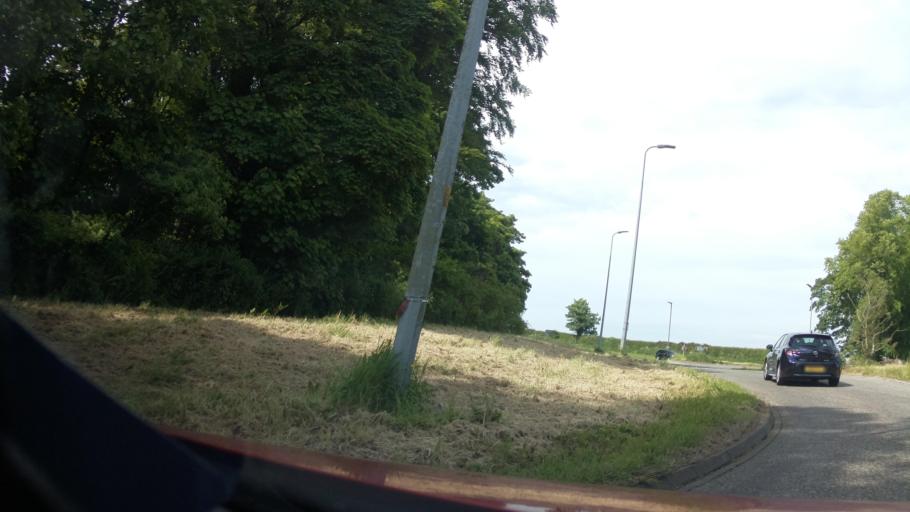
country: GB
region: England
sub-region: Northumberland
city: Alnwick
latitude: 55.4268
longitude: -1.7021
